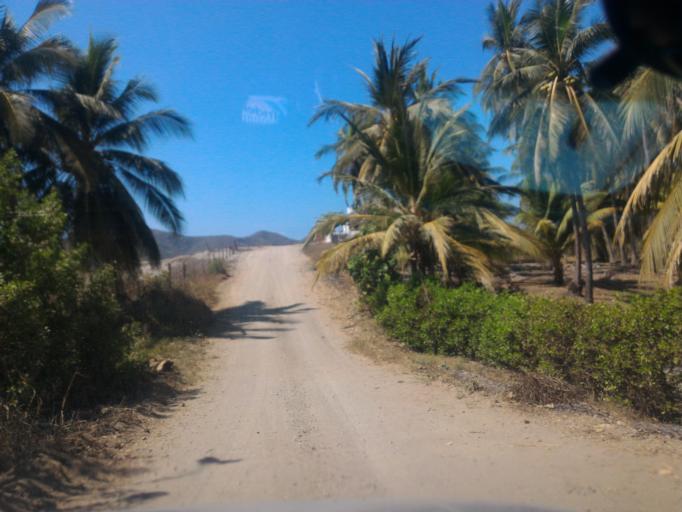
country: MX
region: Michoacan
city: Coahuayana Viejo
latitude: 18.5900
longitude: -103.6856
